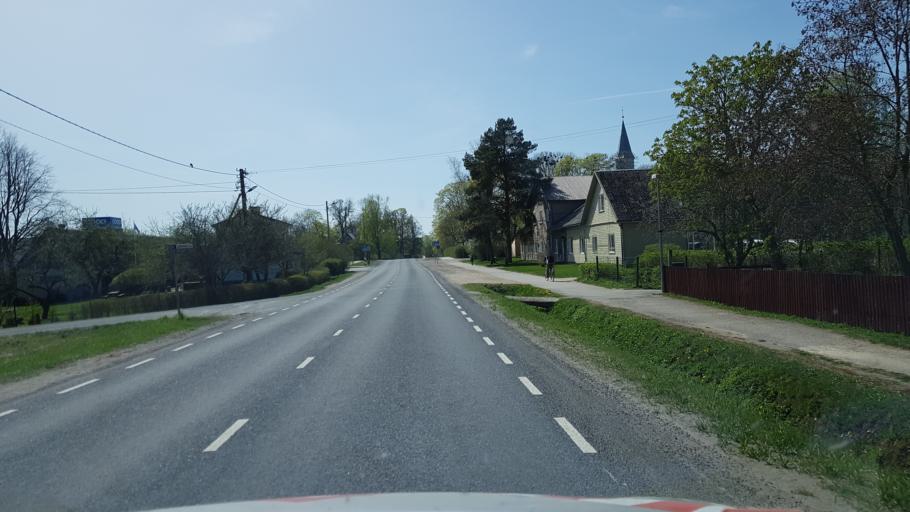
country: EE
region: Tartu
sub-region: Noo vald
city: Noo
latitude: 58.2785
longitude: 26.5379
